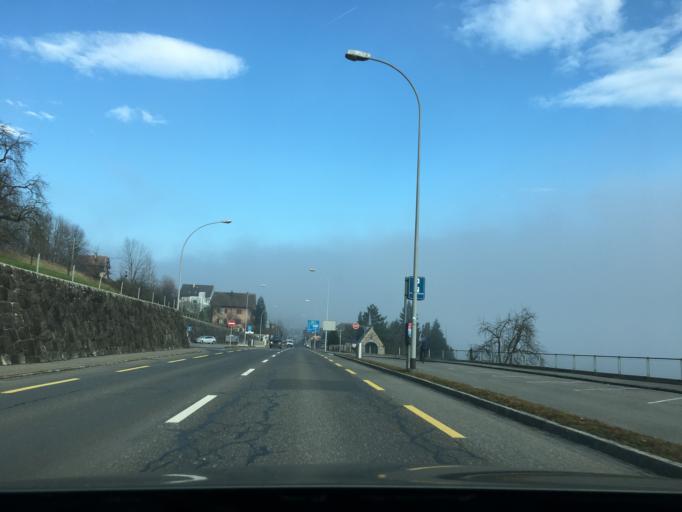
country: CH
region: Schwyz
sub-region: Bezirk Kuessnacht
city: Kussnacht
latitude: 47.0781
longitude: 8.4296
